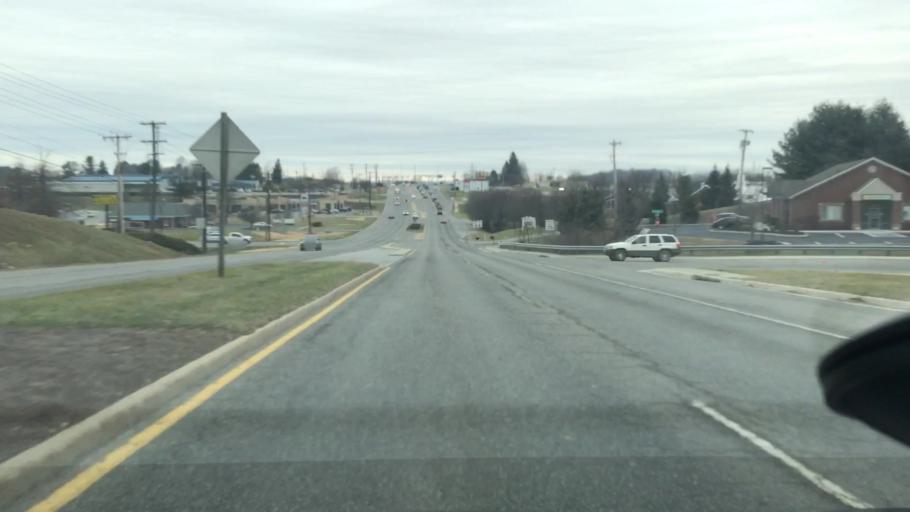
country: US
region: Virginia
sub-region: Montgomery County
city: Christiansburg
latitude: 37.1474
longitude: -80.4149
